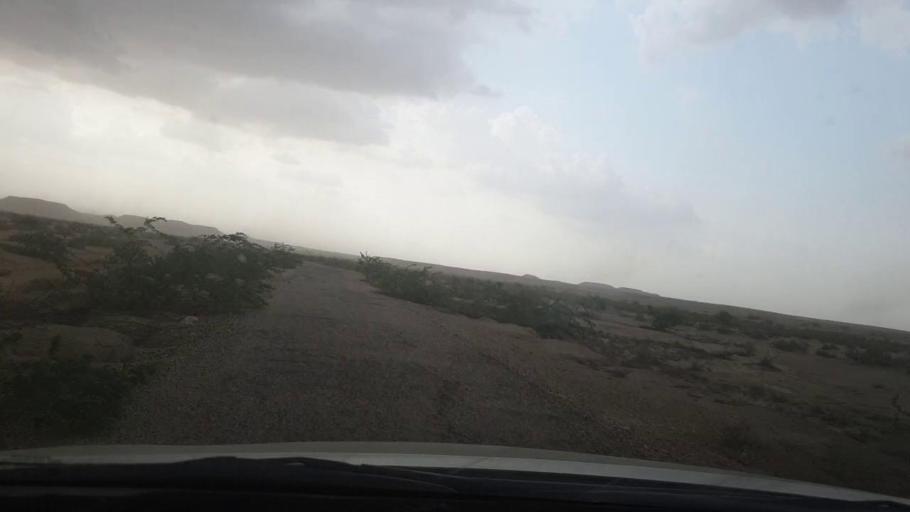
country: PK
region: Sindh
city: Khairpur
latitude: 27.4411
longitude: 68.9761
